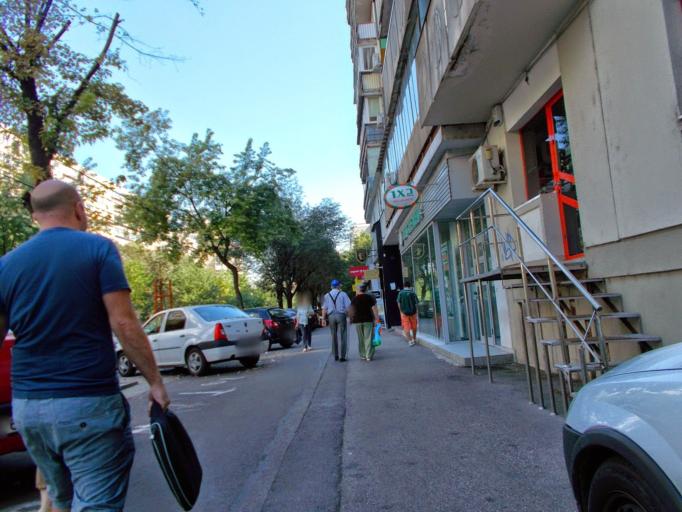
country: RO
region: Bucuresti
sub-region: Municipiul Bucuresti
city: Bucuresti
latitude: 44.3863
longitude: 26.1169
